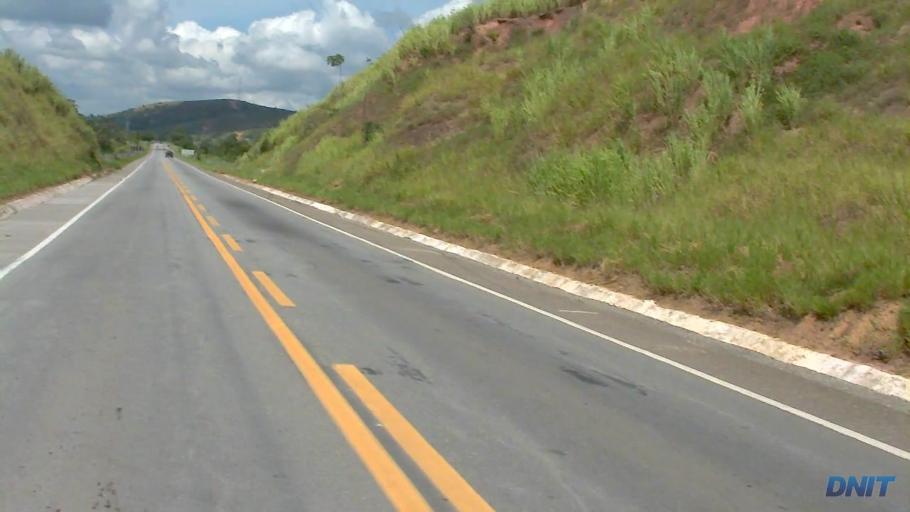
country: BR
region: Minas Gerais
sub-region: Governador Valadares
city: Governador Valadares
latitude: -19.0064
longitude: -42.1322
